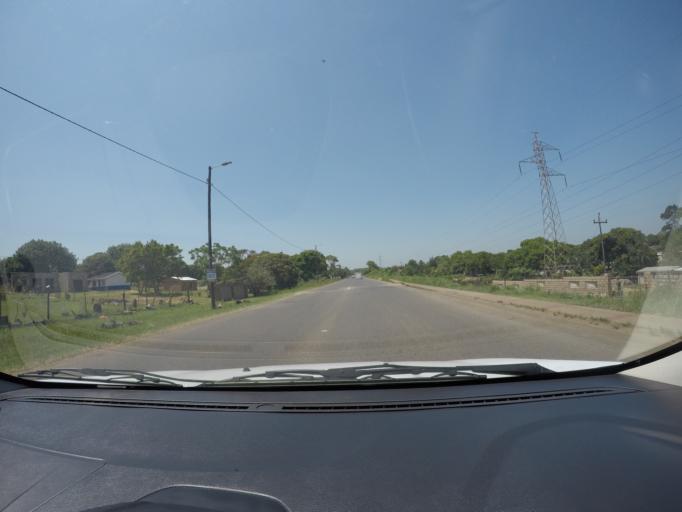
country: ZA
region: KwaZulu-Natal
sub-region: uThungulu District Municipality
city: eSikhawini
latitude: -28.8357
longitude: 31.9384
